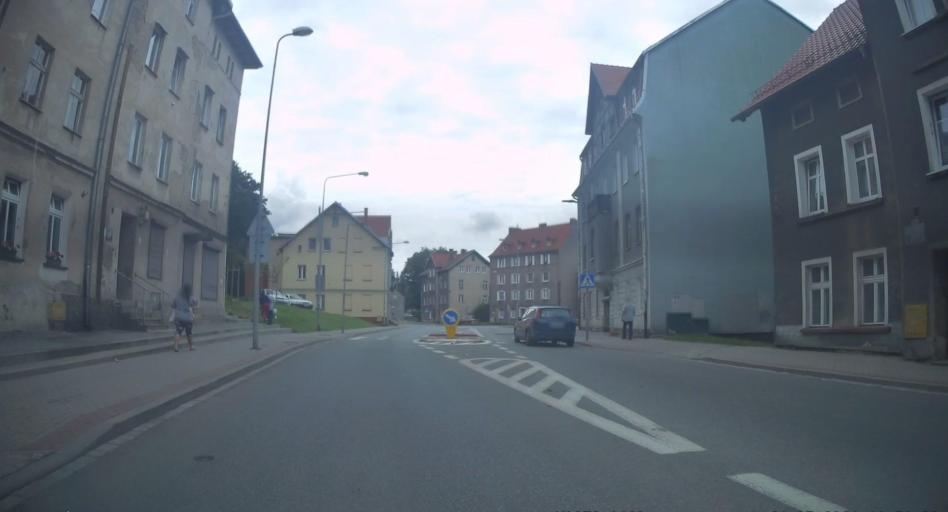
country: PL
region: Lower Silesian Voivodeship
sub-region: Powiat walbrzyski
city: Walbrzych
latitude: 50.7734
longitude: 16.3010
